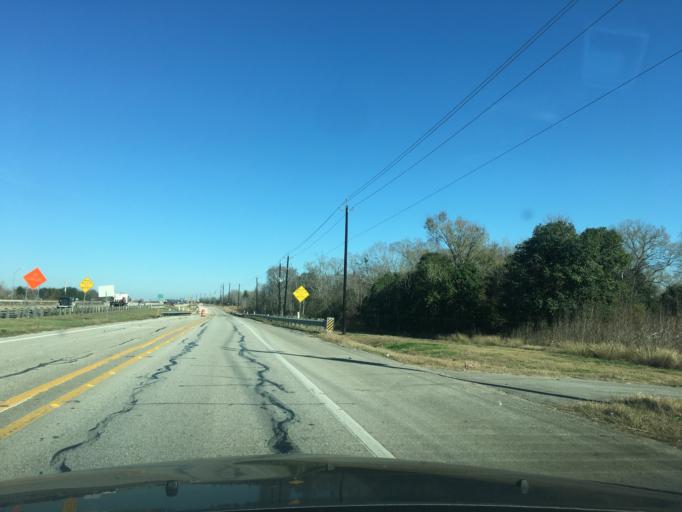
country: US
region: Texas
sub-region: Wharton County
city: East Bernard
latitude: 29.4483
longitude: -95.9947
